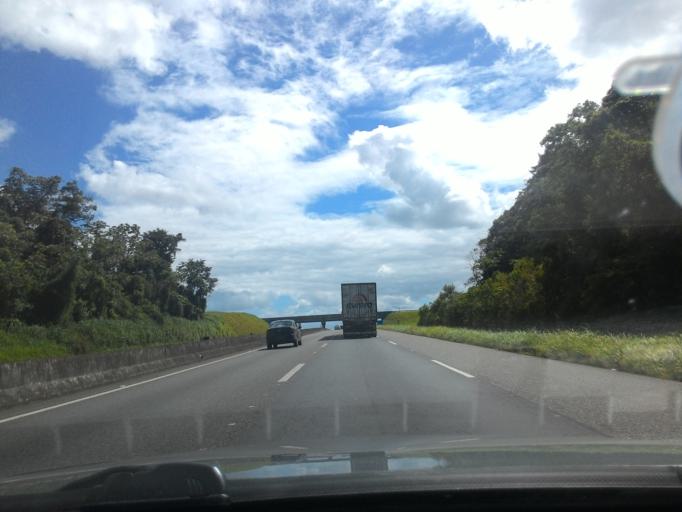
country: BR
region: Sao Paulo
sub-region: Pariquera-Acu
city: Pariquera Acu
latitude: -24.6181
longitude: -47.8911
